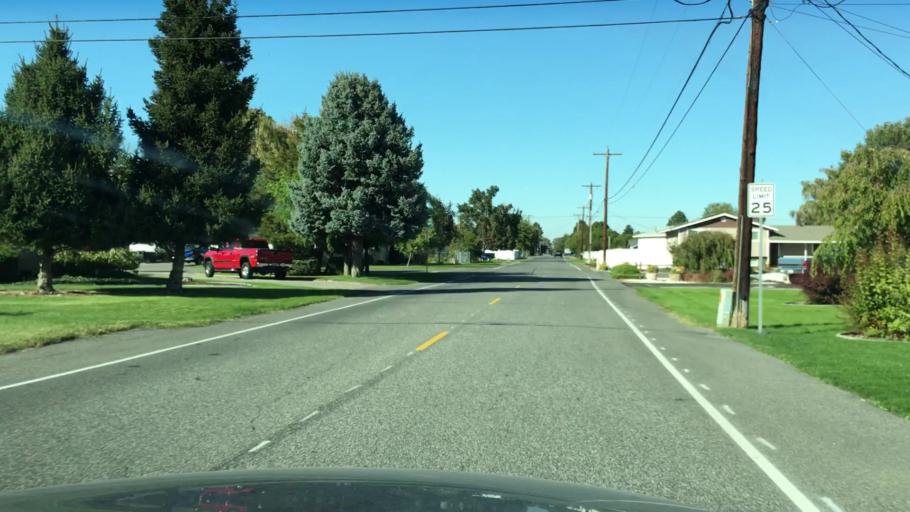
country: US
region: Washington
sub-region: Benton County
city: Kennewick
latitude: 46.2355
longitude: -119.1437
